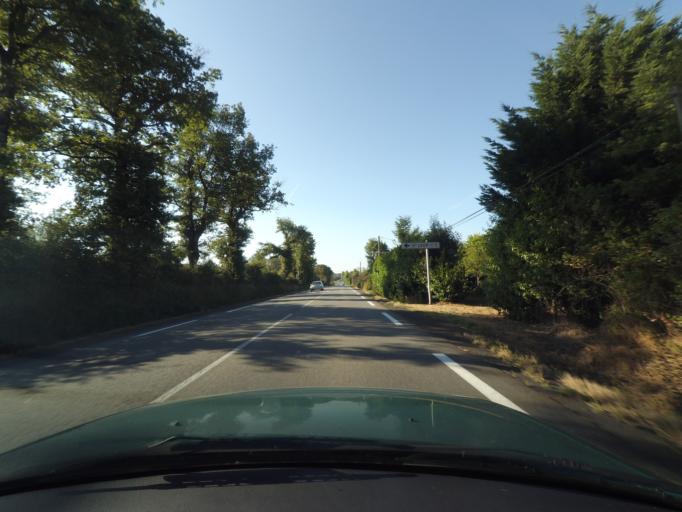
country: FR
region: Poitou-Charentes
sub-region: Departement des Deux-Sevres
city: Chiche
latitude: 46.7498
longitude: -0.3070
